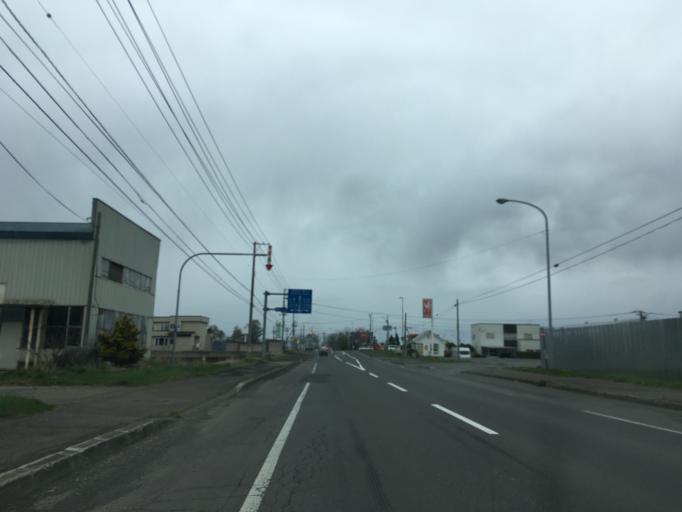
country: JP
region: Hokkaido
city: Chitose
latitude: 42.9488
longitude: 141.8028
